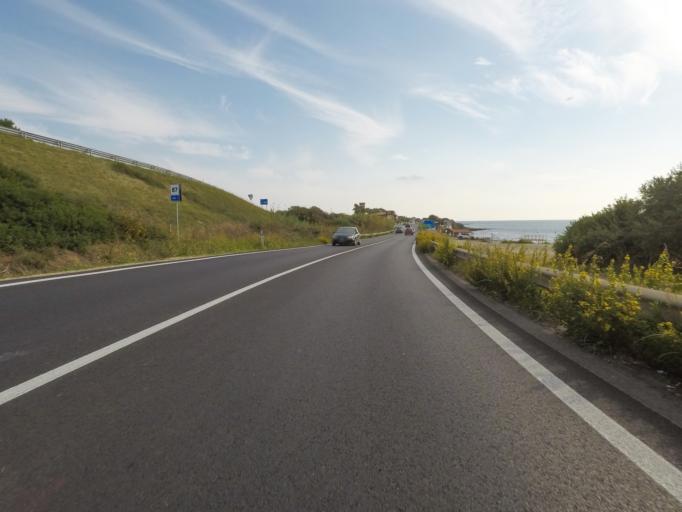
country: IT
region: Latium
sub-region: Citta metropolitana di Roma Capitale
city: Civitavecchia
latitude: 42.0569
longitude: 11.8196
